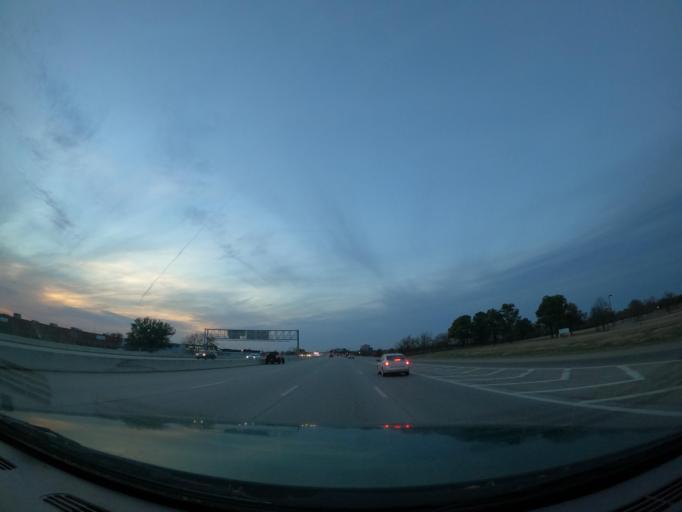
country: US
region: Oklahoma
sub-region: Tulsa County
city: Broken Arrow
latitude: 36.0918
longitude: -95.8409
